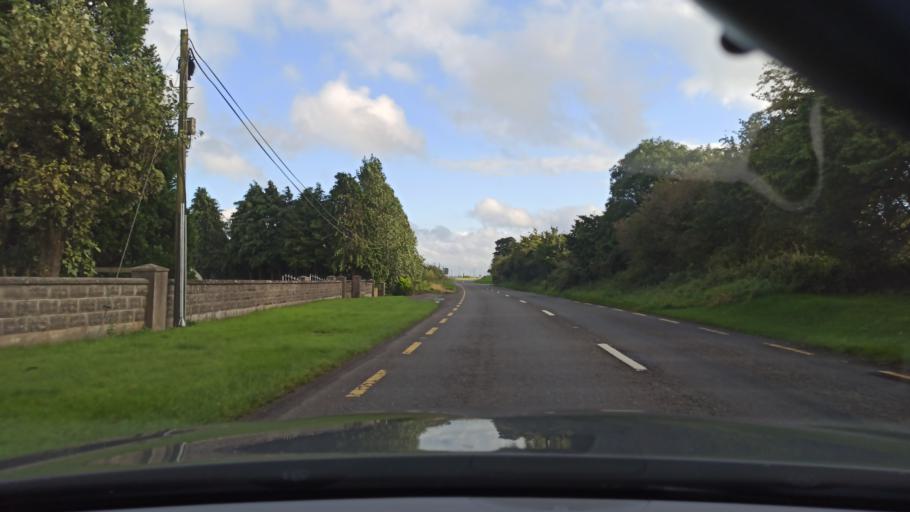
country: IE
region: Munster
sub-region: North Tipperary
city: Roscrea
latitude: 52.9368
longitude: -7.7879
